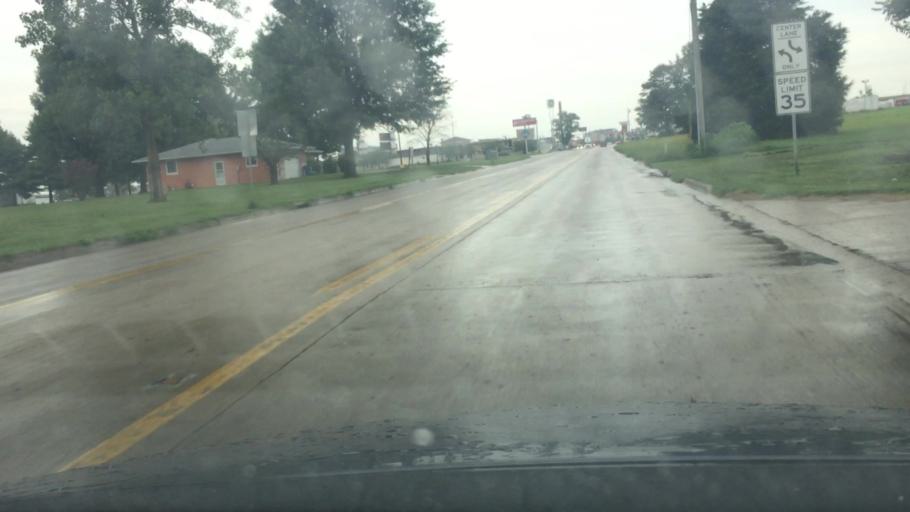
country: US
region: Illinois
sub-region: Williamson County
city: Marion
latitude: 37.7374
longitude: -88.9653
